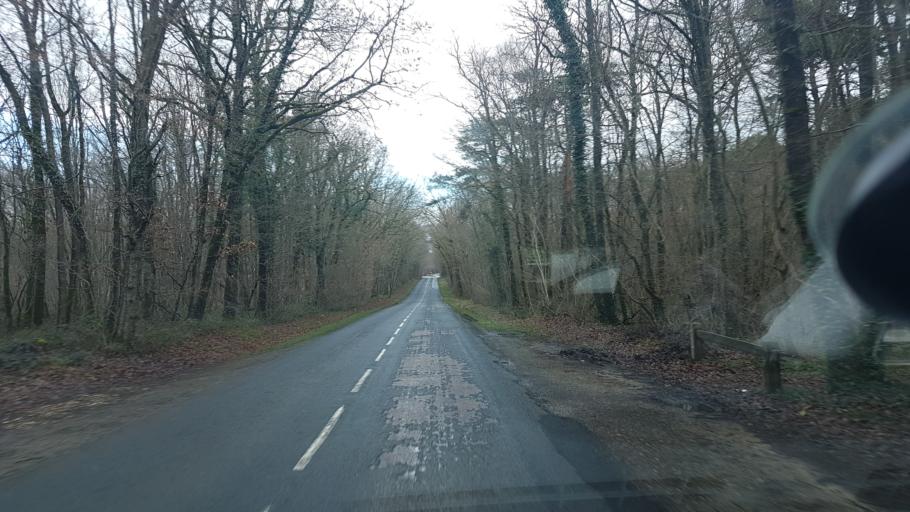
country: FR
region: Ile-de-France
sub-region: Departement de Seine-et-Marne
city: Egreville
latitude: 48.2357
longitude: 2.8079
